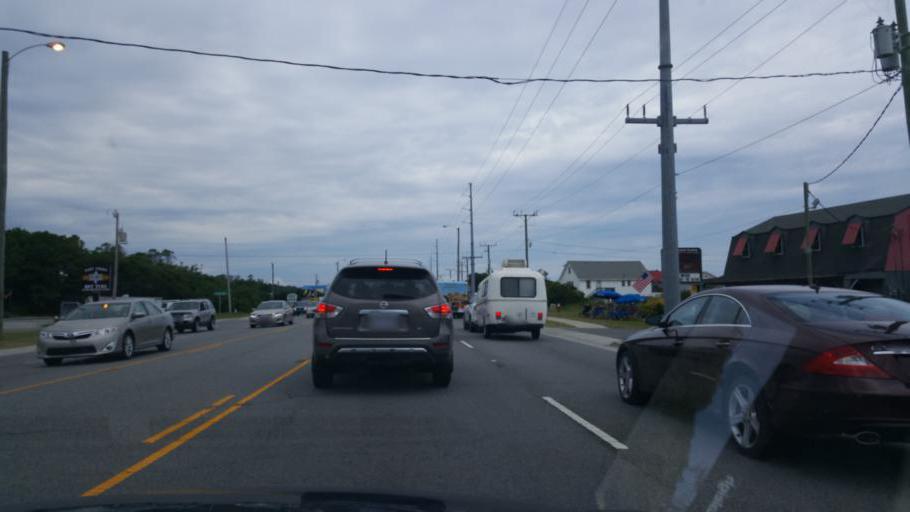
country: US
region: North Carolina
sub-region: Dare County
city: Kill Devil Hills
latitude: 35.9947
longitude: -75.6495
